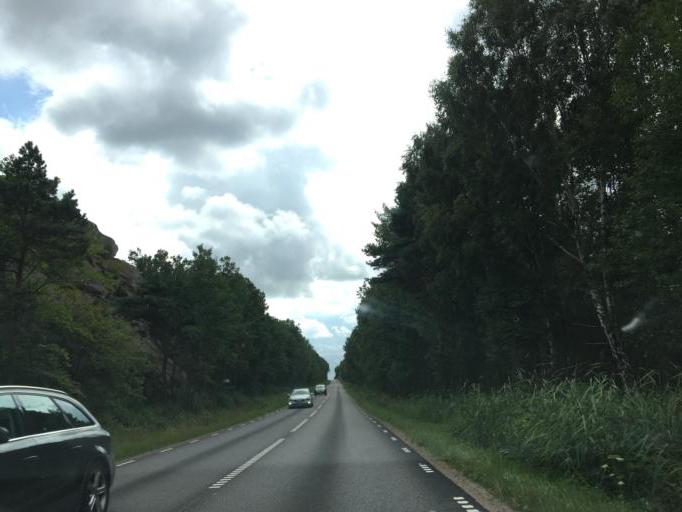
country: SE
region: Vaestra Goetaland
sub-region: Sotenas Kommun
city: Kungshamn
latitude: 58.4041
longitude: 11.2679
